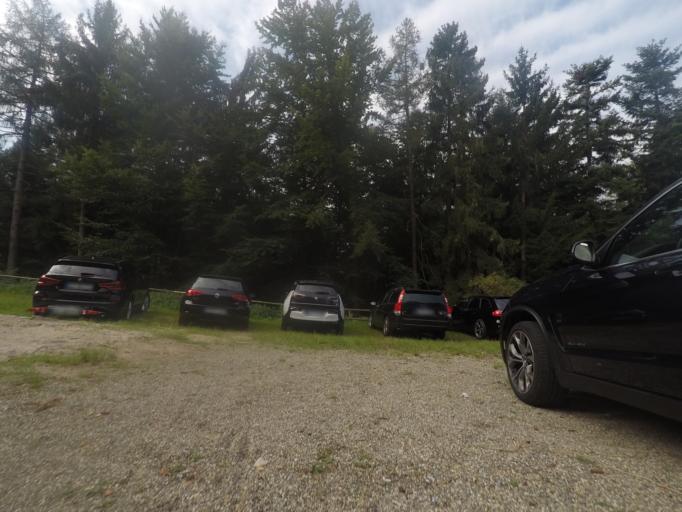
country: DE
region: Baden-Wuerttemberg
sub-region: Karlsruhe Region
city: Malsch
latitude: 48.8429
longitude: 8.3756
